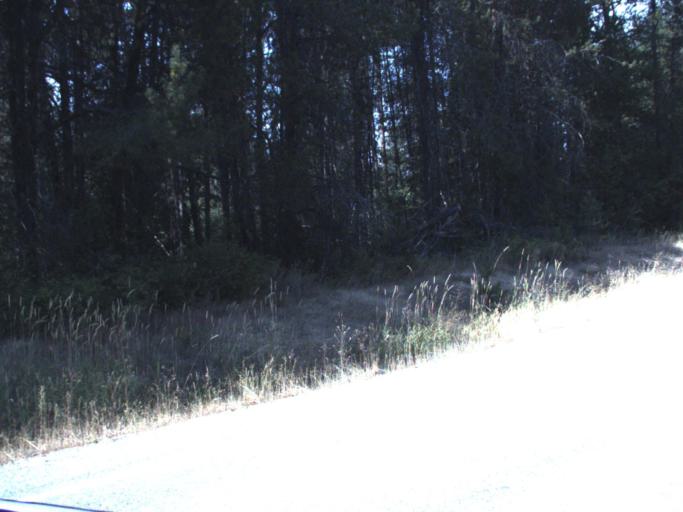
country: US
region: Washington
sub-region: Pend Oreille County
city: Newport
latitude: 48.2037
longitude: -117.2916
